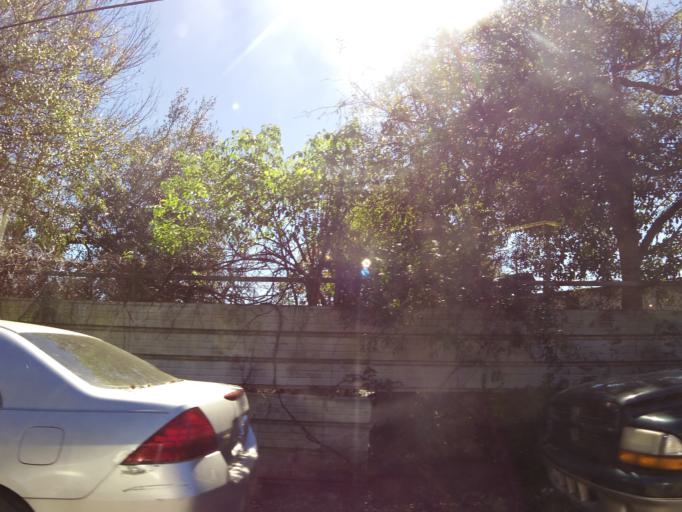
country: US
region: Florida
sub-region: Duval County
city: Jacksonville
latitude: 30.3225
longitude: -81.7184
